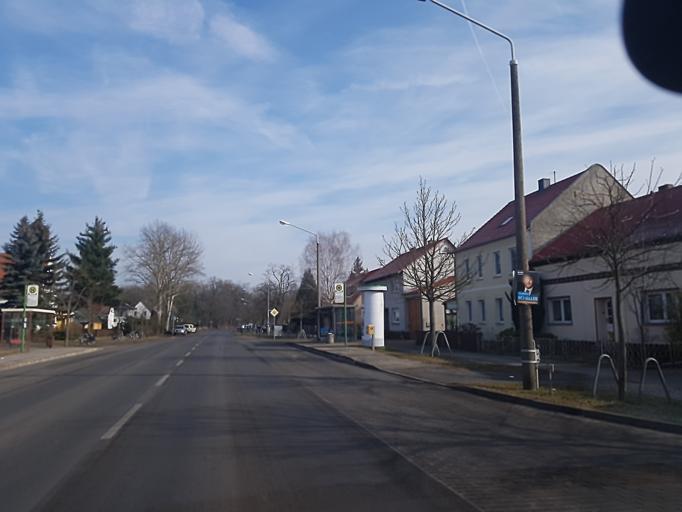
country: DE
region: Brandenburg
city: Brandenburg an der Havel
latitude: 52.3719
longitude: 12.5040
